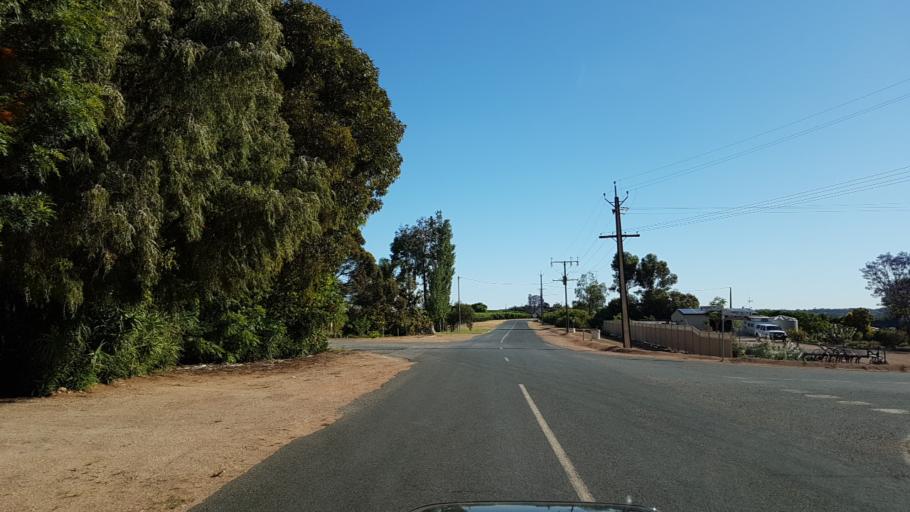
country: AU
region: South Australia
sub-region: Loxton Waikerie
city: Waikerie
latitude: -34.1703
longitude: 140.0325
